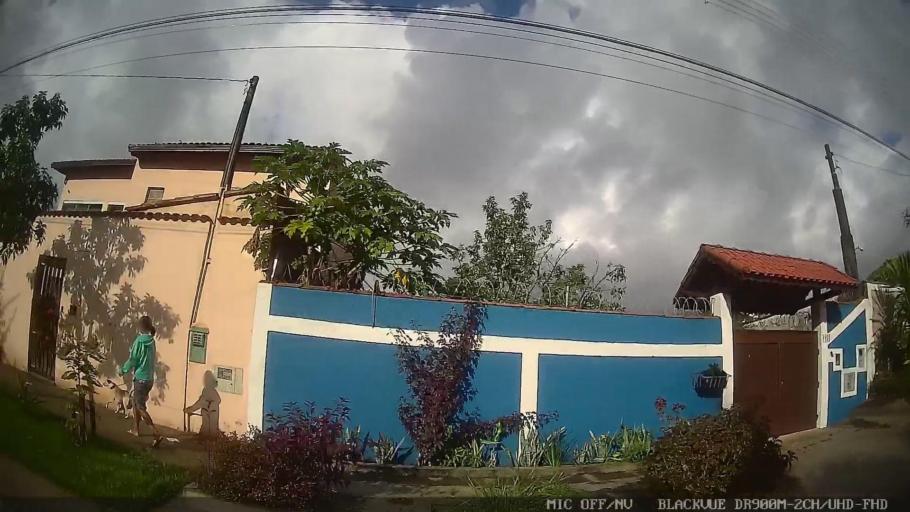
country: BR
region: Sao Paulo
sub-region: Itanhaem
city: Itanhaem
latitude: -24.1938
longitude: -46.8651
